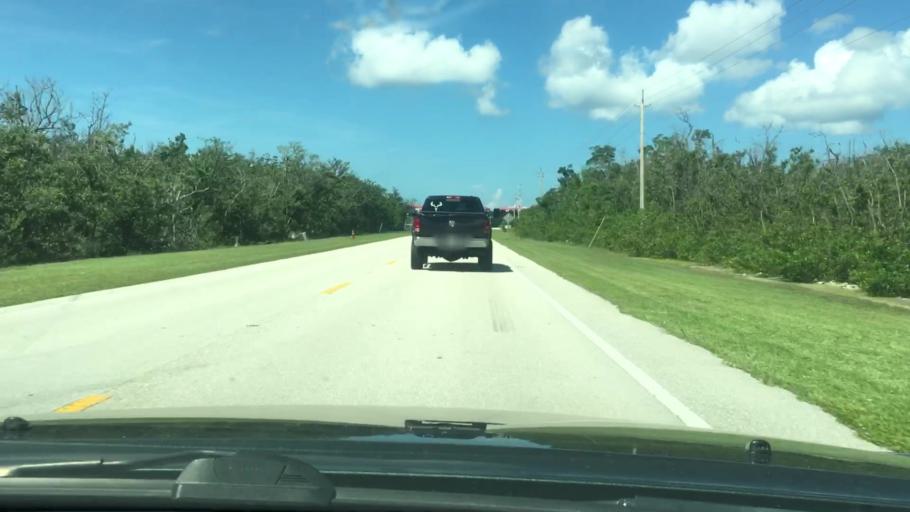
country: US
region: Florida
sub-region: Collier County
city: Marco
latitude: 25.9319
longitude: -81.6689
